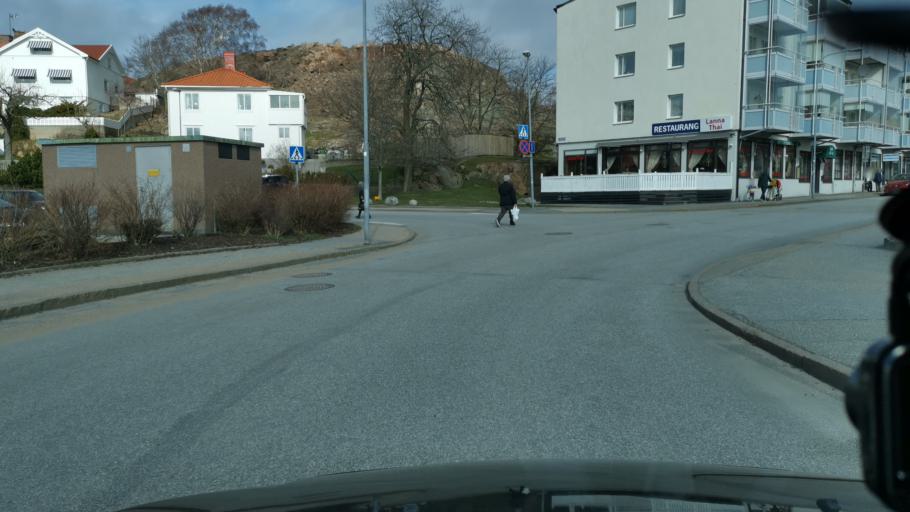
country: SE
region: Vaestra Goetaland
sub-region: Lysekils Kommun
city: Lysekil
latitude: 58.2765
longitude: 11.4414
